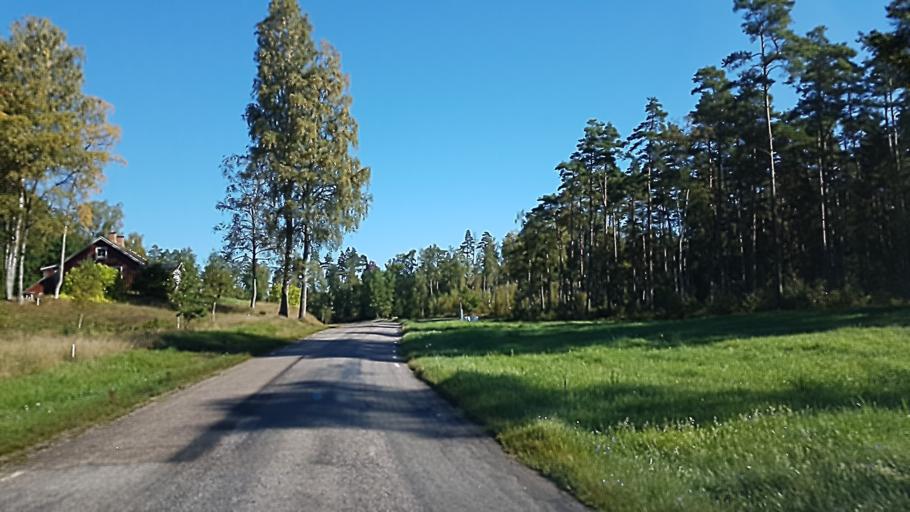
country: SE
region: Kronoberg
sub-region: Ljungby Kommun
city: Ljungby
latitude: 56.8139
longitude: 14.0360
